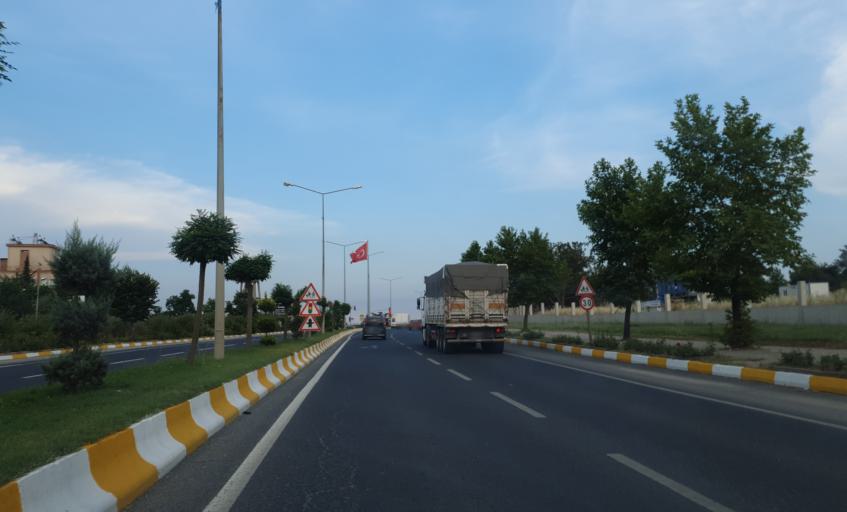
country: TR
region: Kirklareli
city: Luleburgaz
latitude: 41.3998
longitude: 27.3745
